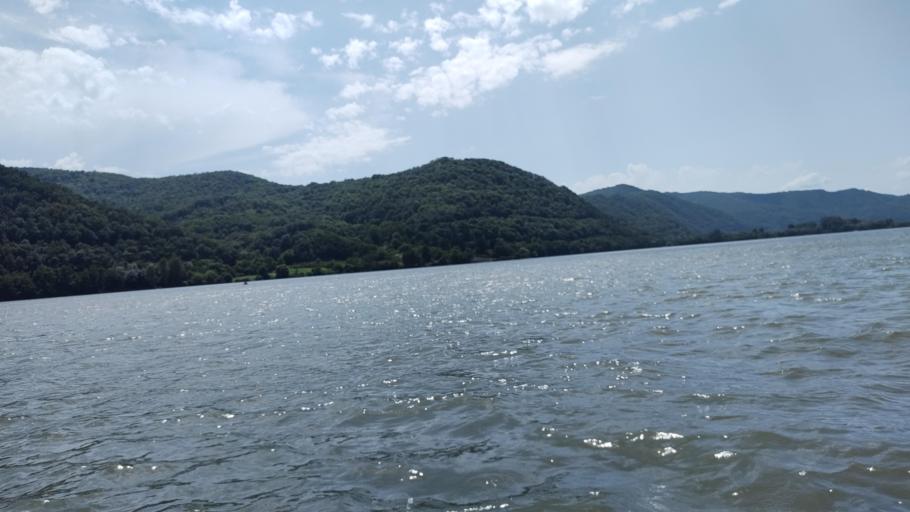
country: RO
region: Caras-Severin
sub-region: Comuna Berzasca
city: Liubcova
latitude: 44.6513
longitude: 21.8625
